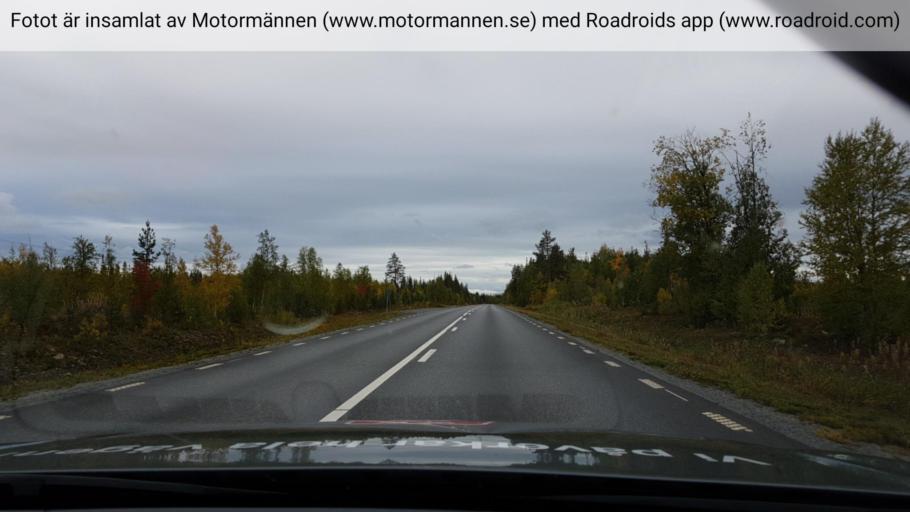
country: SE
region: Vaesterbotten
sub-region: Dorotea Kommun
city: Dorotea
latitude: 64.3184
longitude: 16.6109
